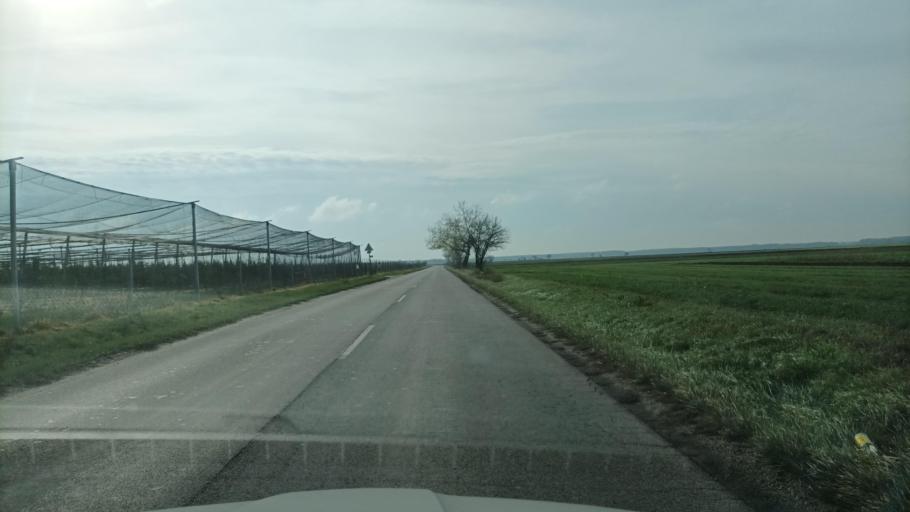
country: HU
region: Pest
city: Rackeve
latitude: 47.1148
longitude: 18.9418
